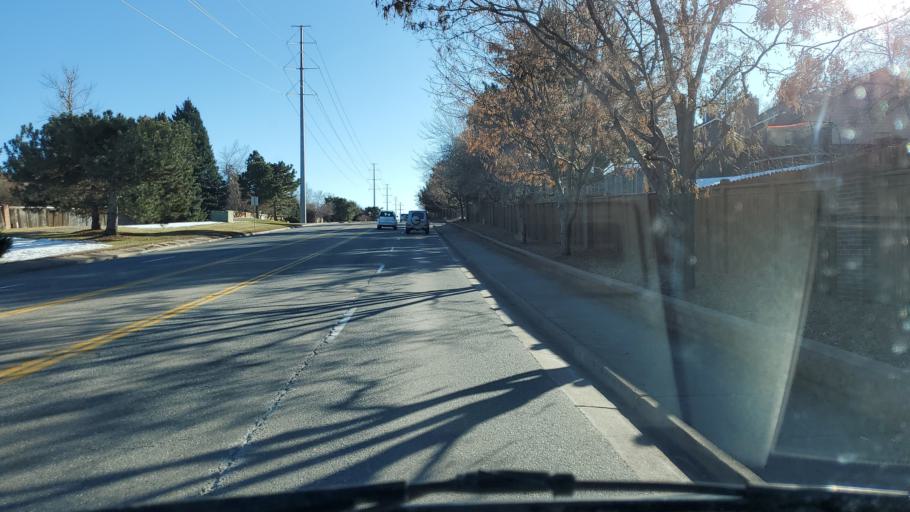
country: US
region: Colorado
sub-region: Arapahoe County
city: Castlewood
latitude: 39.5741
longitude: -104.9044
